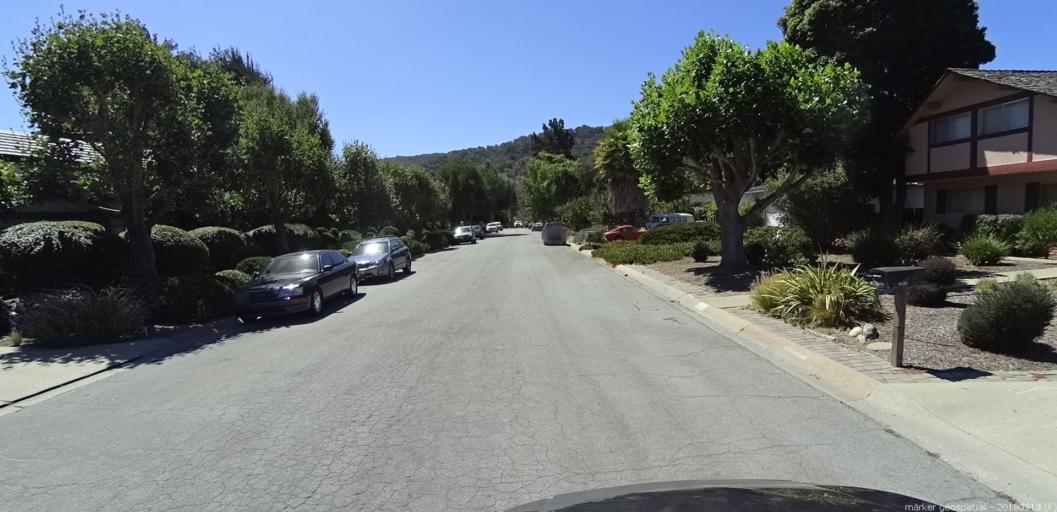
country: US
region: California
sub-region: Monterey County
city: Carmel Valley Village
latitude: 36.5220
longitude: -121.8112
